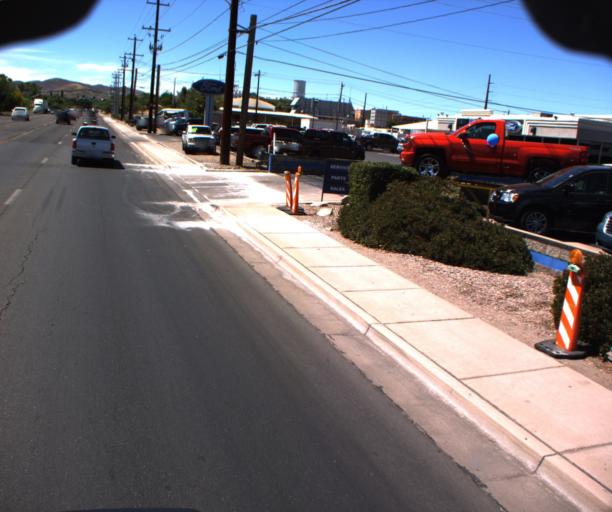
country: US
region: Arizona
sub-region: Santa Cruz County
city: Nogales
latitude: 31.3650
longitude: -110.9309
